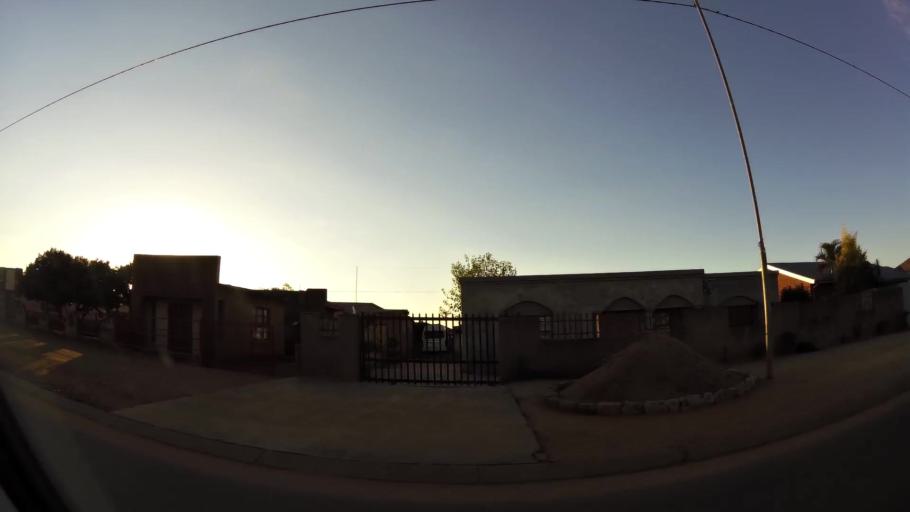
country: ZA
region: Limpopo
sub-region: Waterberg District Municipality
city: Mokopane
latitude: -24.1432
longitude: 28.9919
